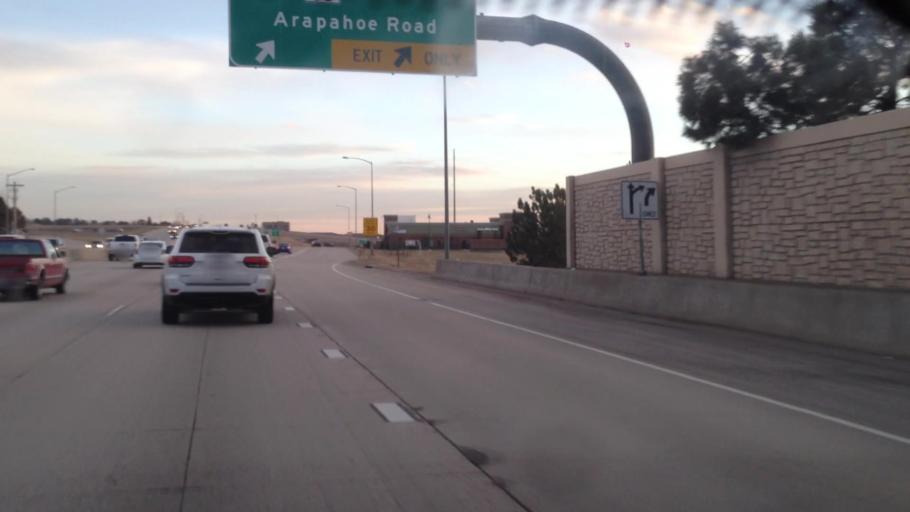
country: US
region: Colorado
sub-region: Arapahoe County
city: Dove Valley
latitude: 39.5990
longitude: -104.8047
